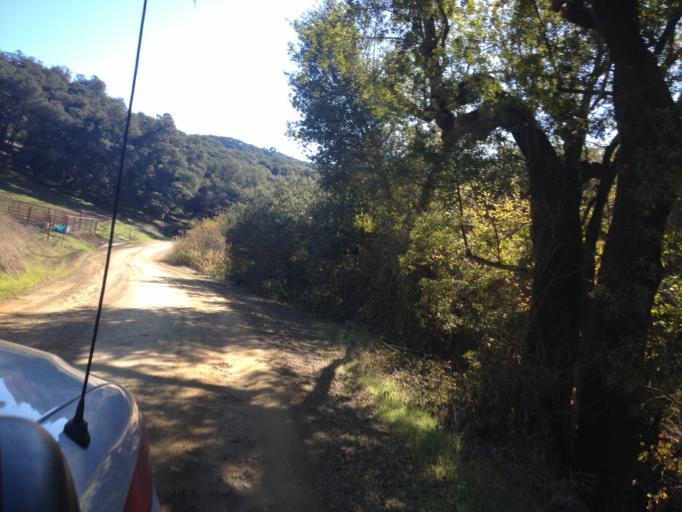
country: US
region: California
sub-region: San Luis Obispo County
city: Avila Beach
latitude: 35.2469
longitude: -120.7771
